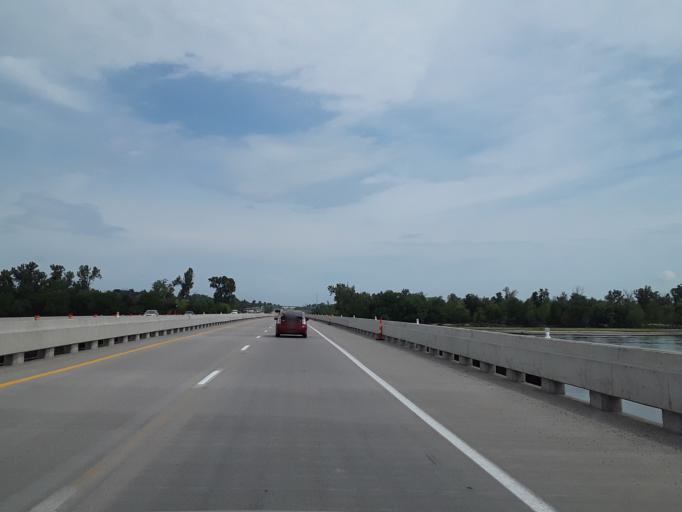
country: US
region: Nebraska
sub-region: Sarpy County
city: Offutt Air Force Base
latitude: 41.0571
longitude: -95.9276
